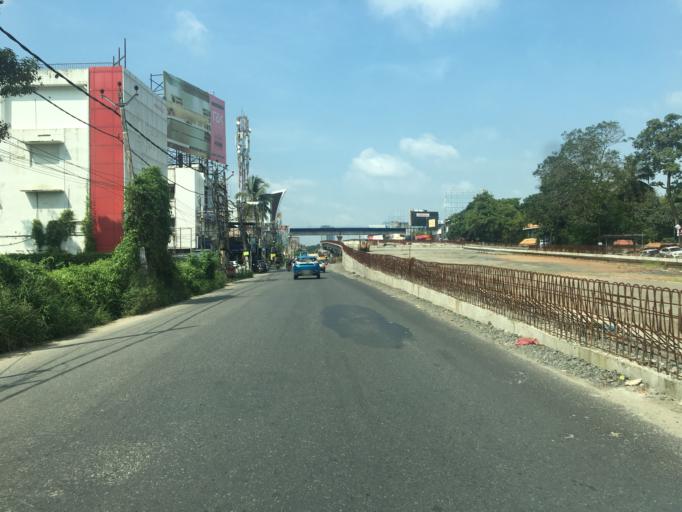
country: IN
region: Kerala
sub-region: Ernakulam
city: Cochin
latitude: 9.9656
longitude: 76.3182
